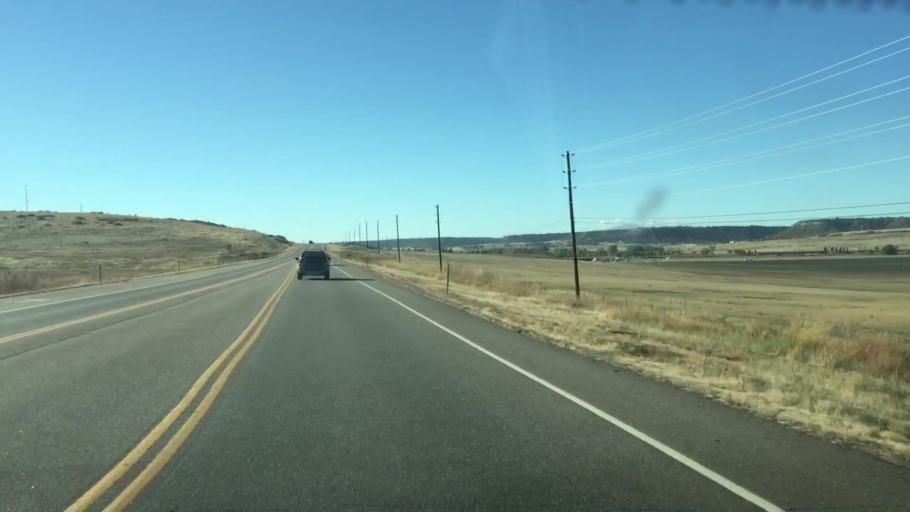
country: US
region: Colorado
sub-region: Douglas County
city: The Pinery
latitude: 39.4274
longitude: -104.7606
